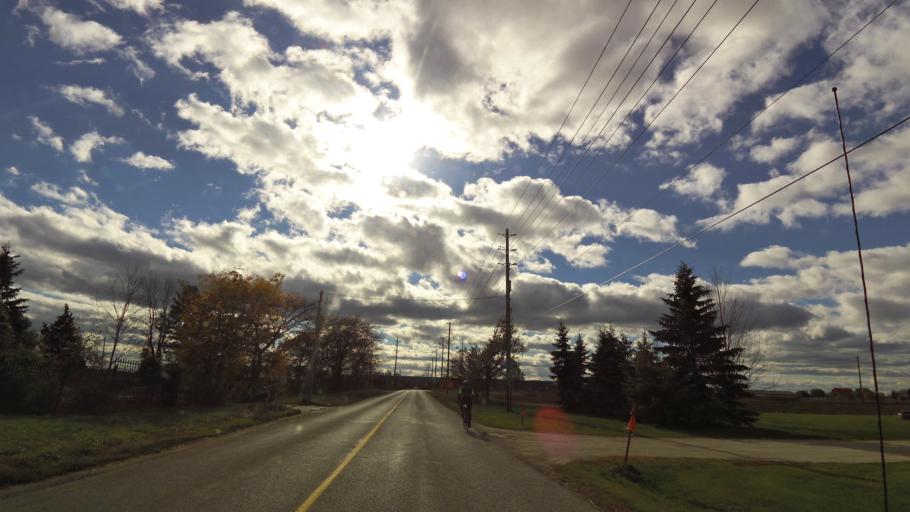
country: CA
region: Ontario
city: Burlington
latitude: 43.4585
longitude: -79.8171
